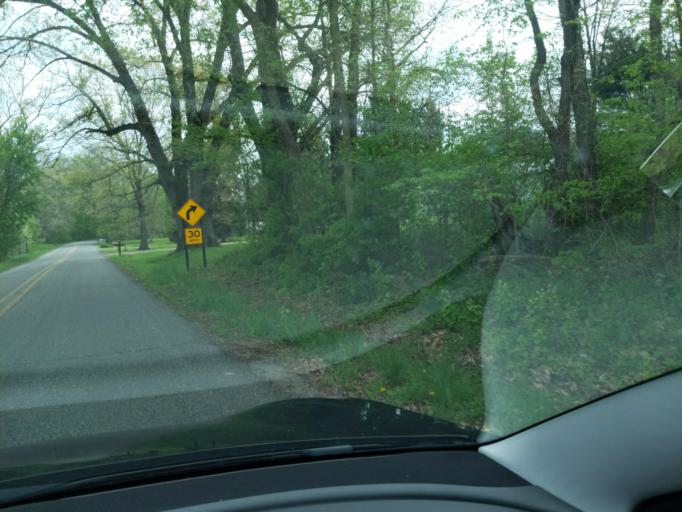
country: US
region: Michigan
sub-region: Ingham County
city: Leslie
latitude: 42.4985
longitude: -84.3299
